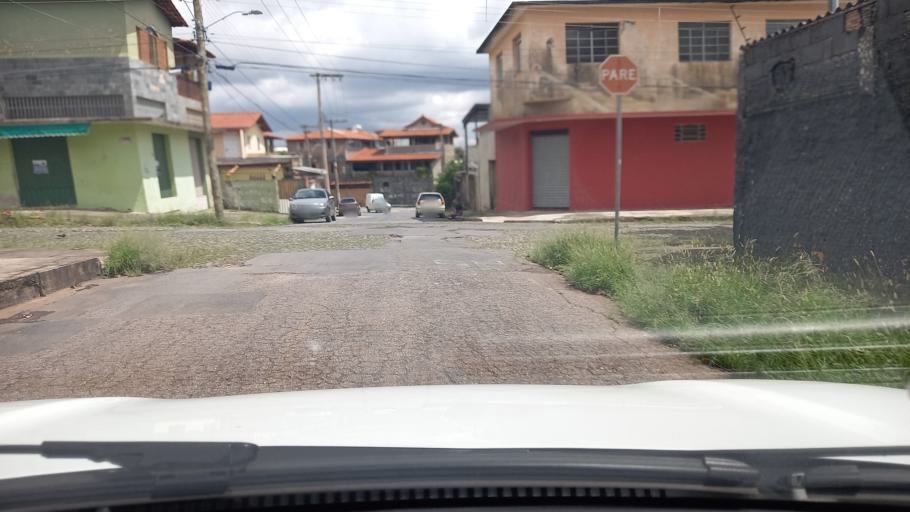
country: BR
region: Minas Gerais
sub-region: Contagem
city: Contagem
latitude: -19.9013
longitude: -44.0132
